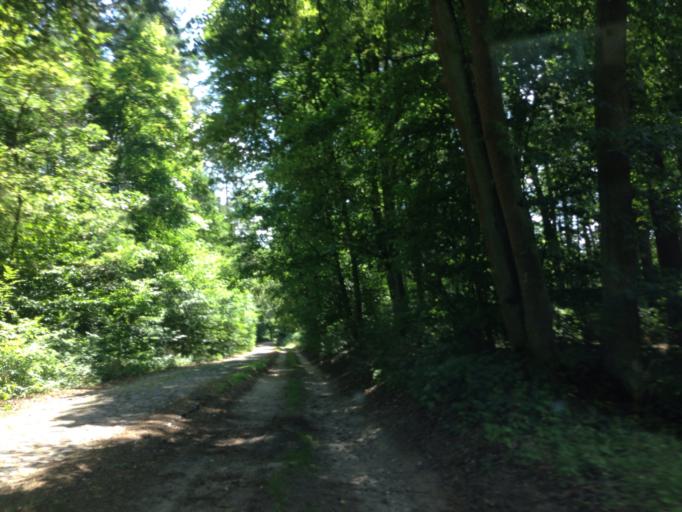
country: PL
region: Kujawsko-Pomorskie
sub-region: Powiat brodnicki
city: Gorzno
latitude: 53.2285
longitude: 19.6559
